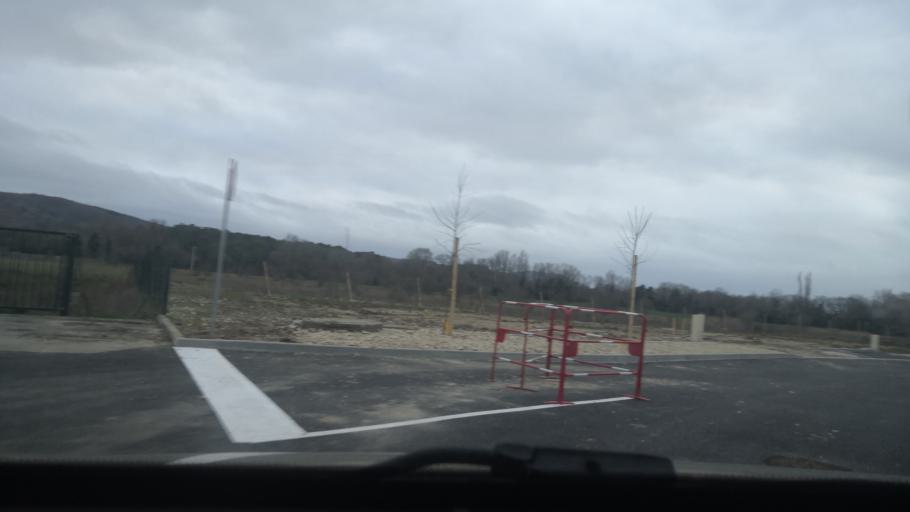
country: FR
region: Rhone-Alpes
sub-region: Departement de la Drome
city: Montboucher-sur-Jabron
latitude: 44.5517
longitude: 4.8633
